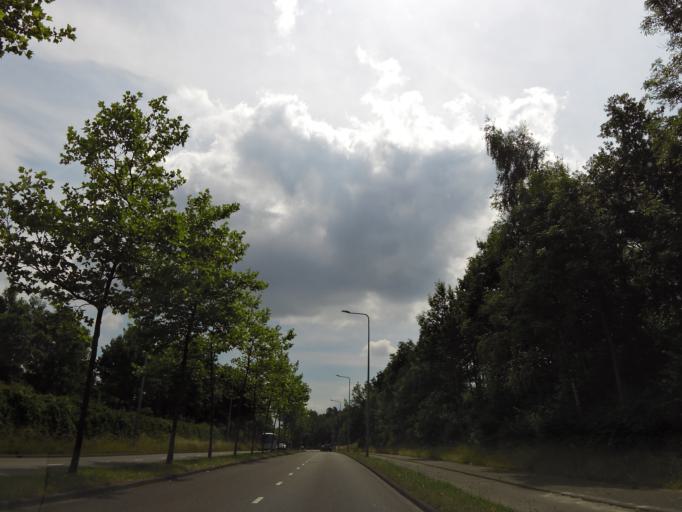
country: NL
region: Limburg
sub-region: Gemeente Heerlen
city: Heerlen
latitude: 50.8991
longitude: 5.9654
